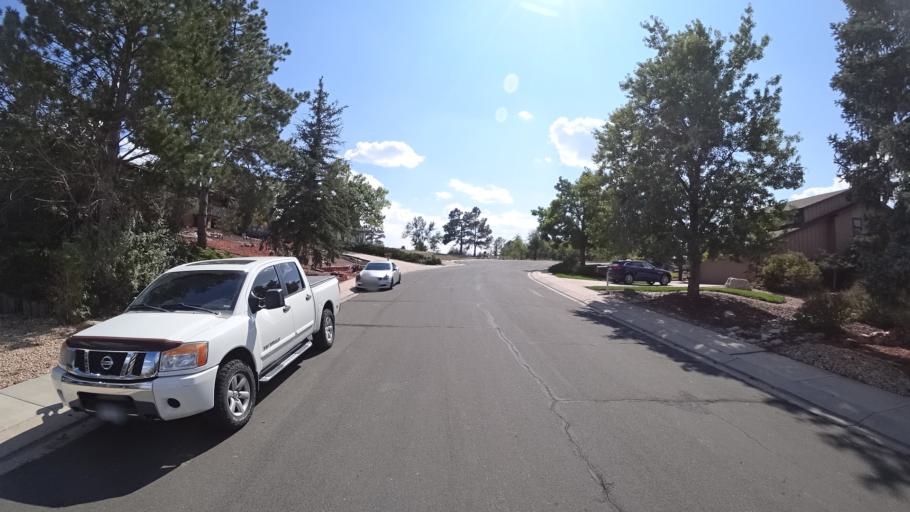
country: US
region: Colorado
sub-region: El Paso County
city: Cimarron Hills
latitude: 38.8699
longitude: -104.7456
